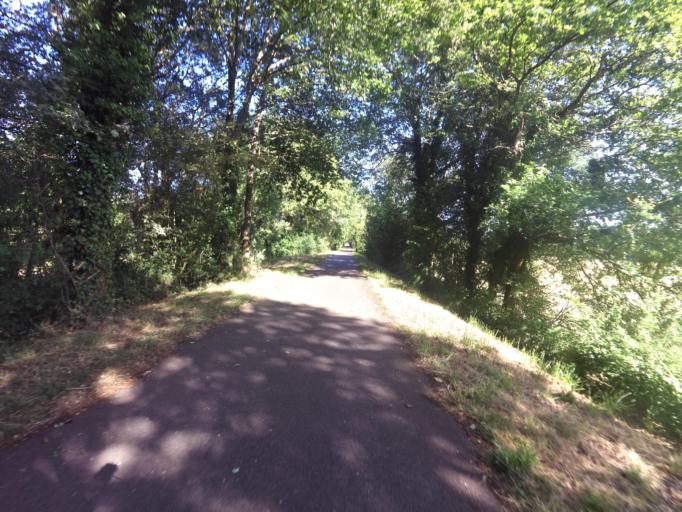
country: FR
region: Brittany
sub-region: Departement du Morbihan
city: Malestroit
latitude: 47.8394
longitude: -2.4311
